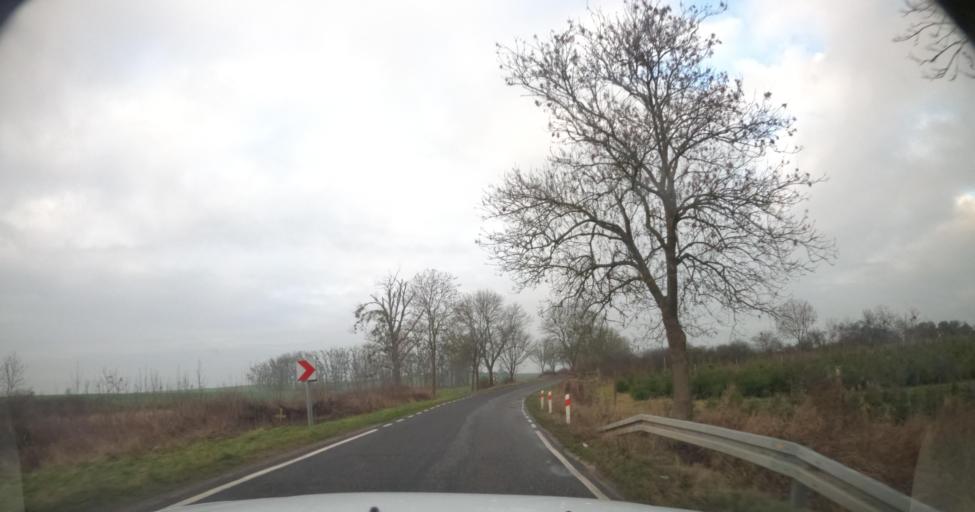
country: PL
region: West Pomeranian Voivodeship
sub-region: Powiat mysliborski
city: Debno
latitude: 52.7348
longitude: 14.6427
